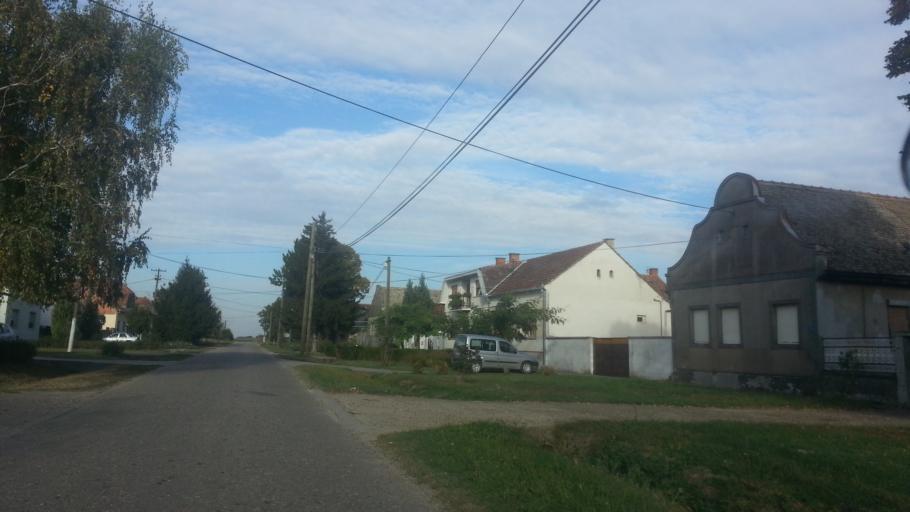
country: RS
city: Belegis
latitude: 45.0257
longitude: 20.3428
